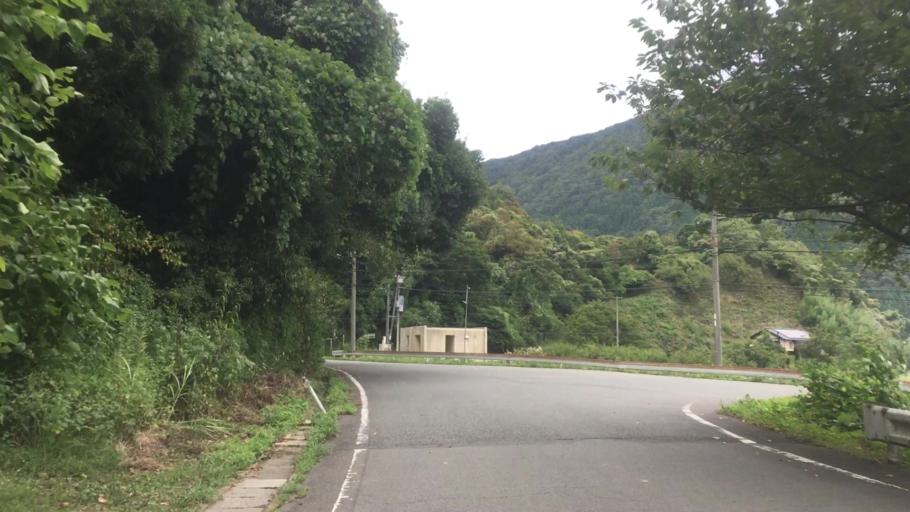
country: JP
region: Hyogo
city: Toyooka
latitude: 35.6040
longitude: 134.8002
